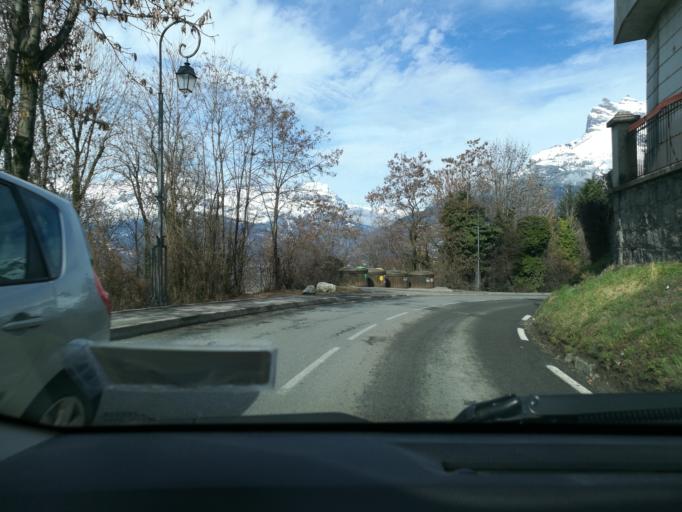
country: FR
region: Rhone-Alpes
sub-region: Departement de la Haute-Savoie
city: Saint-Gervais-les-Bains
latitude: 45.8970
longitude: 6.7092
